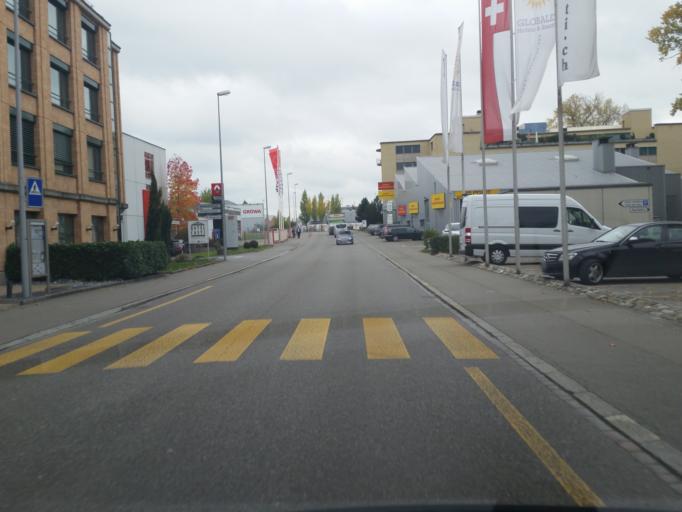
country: CH
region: Zurich
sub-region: Bezirk Dietikon
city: Dietikon / Vorstadt
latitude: 47.4127
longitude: 8.4024
